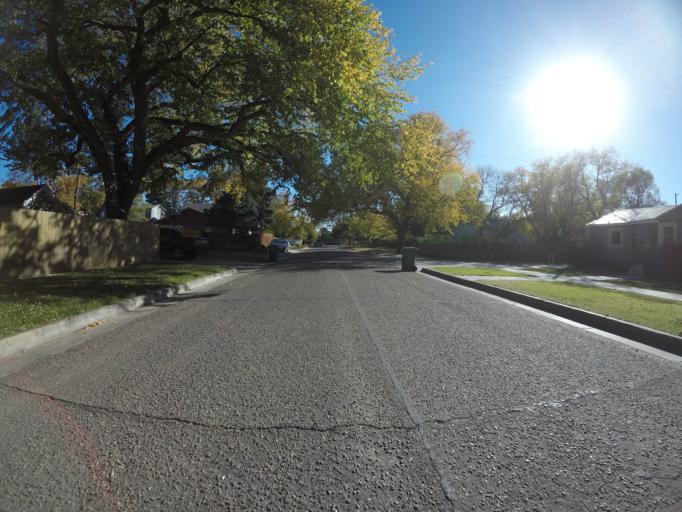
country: US
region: Kansas
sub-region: Thomas County
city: Colby
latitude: 39.3978
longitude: -101.0531
